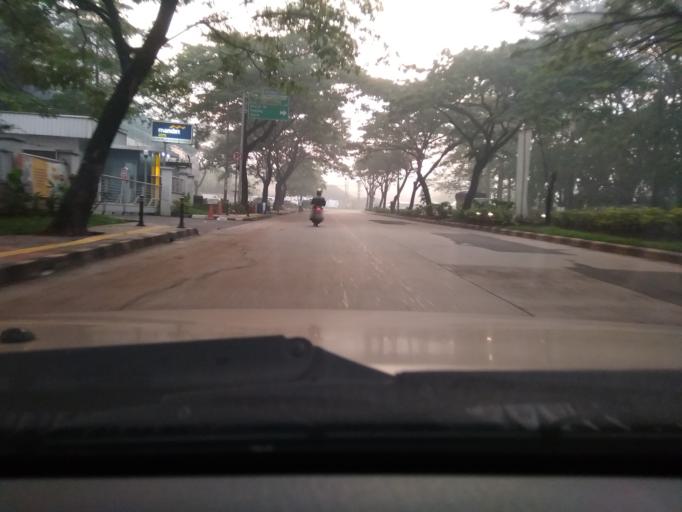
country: ID
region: West Java
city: Serpong
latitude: -6.3279
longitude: 106.6836
